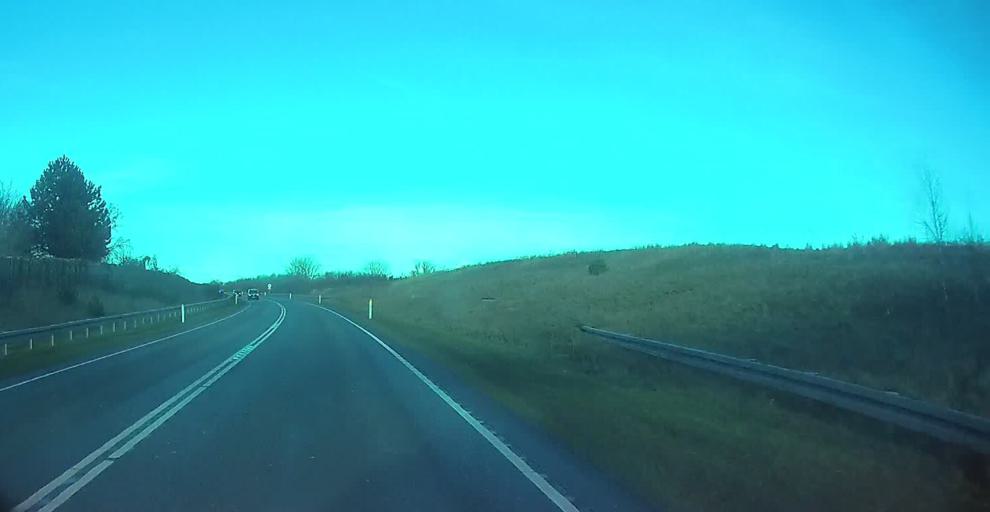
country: DK
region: Capital Region
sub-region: Frederikssund Kommune
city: Slangerup
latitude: 55.8819
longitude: 12.2047
